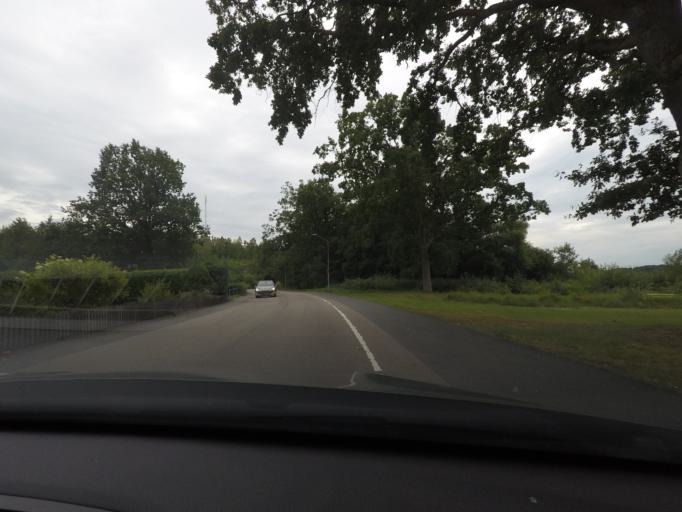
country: SE
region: Skane
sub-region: Osby Kommun
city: Osby
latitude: 56.3741
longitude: 14.0032
